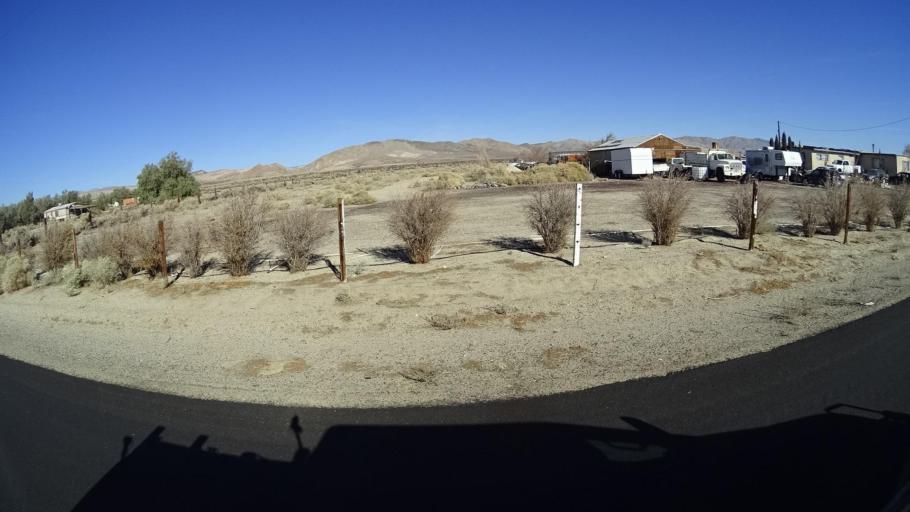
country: US
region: California
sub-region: Kern County
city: California City
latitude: 35.3085
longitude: -117.9537
